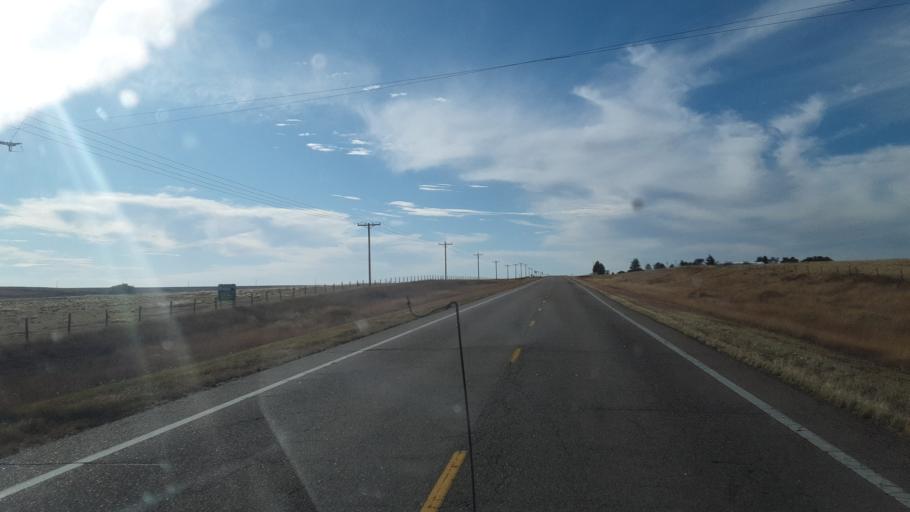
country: US
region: Kansas
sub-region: Finney County
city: Garden City
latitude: 38.0601
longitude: -100.6016
